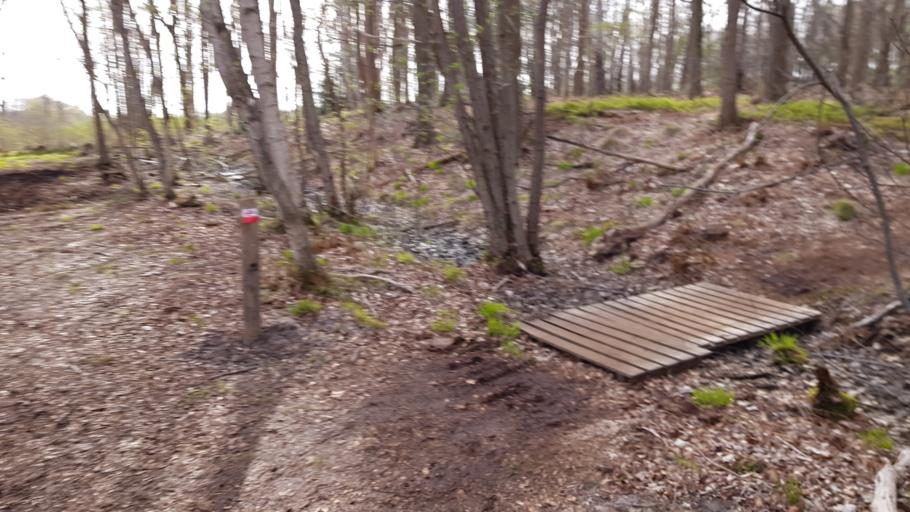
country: NL
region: Gelderland
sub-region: Gemeente Barneveld
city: Terschuur
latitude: 52.1796
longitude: 5.5428
